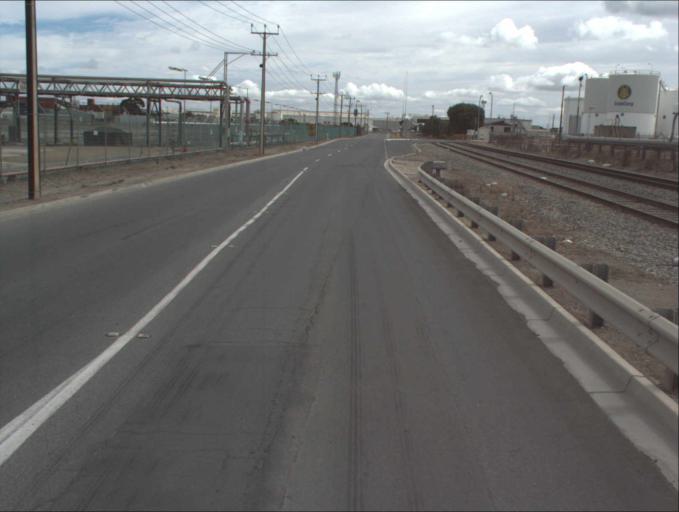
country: AU
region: South Australia
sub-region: Port Adelaide Enfield
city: Birkenhead
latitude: -34.8282
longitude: 138.5046
